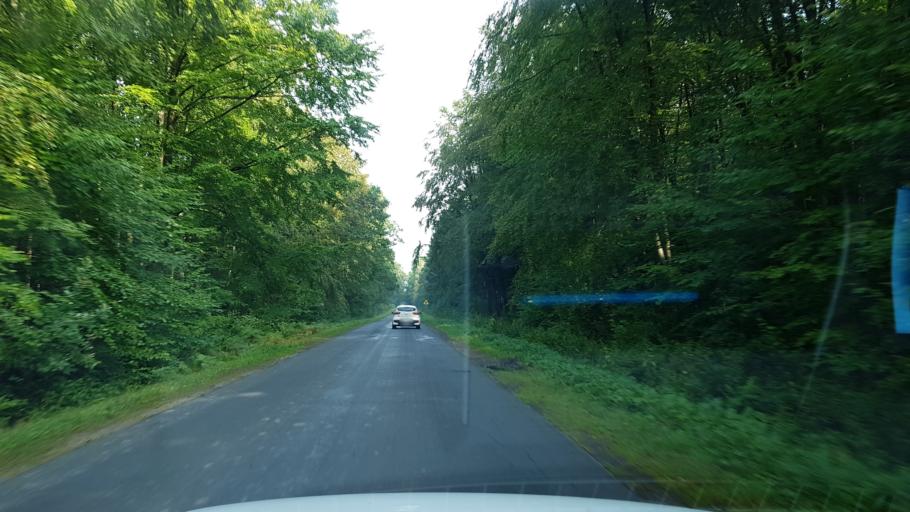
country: PL
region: West Pomeranian Voivodeship
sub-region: Powiat slawienski
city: Slawno
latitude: 54.4136
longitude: 16.6151
